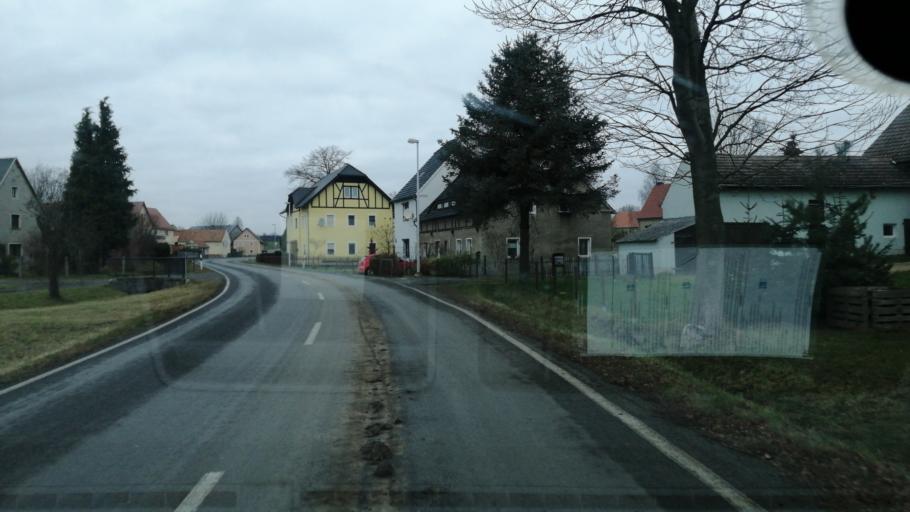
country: DE
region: Saxony
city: Sohland am Rotstein
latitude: 51.0687
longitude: 14.7813
